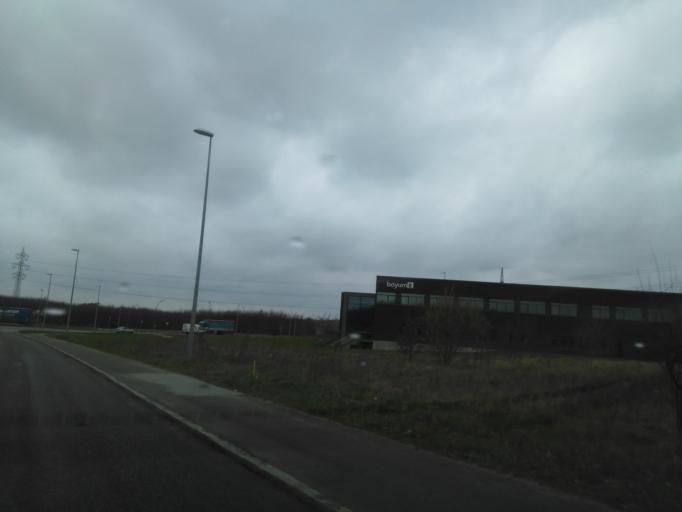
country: DK
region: Central Jutland
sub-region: Arhus Kommune
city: Stavtrup
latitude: 56.1647
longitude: 10.0969
